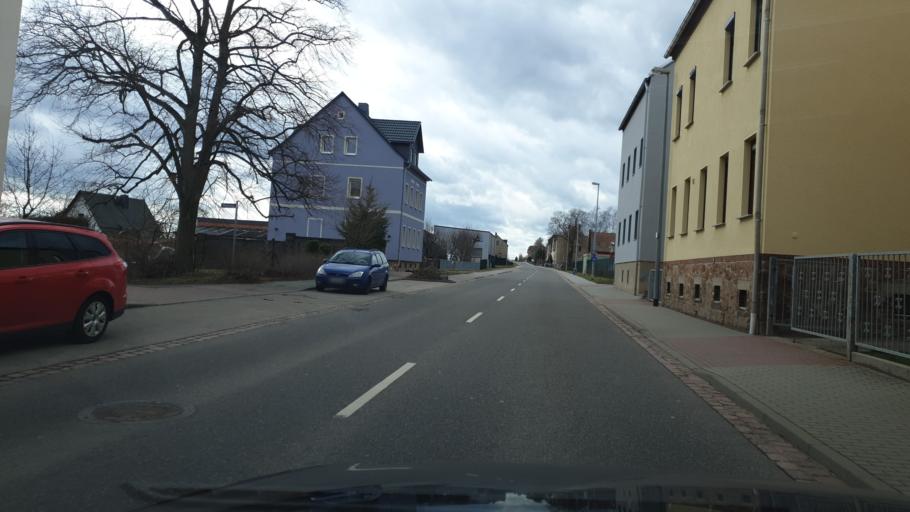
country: DE
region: Saxony
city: Mittweida
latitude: 50.9861
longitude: 12.9563
